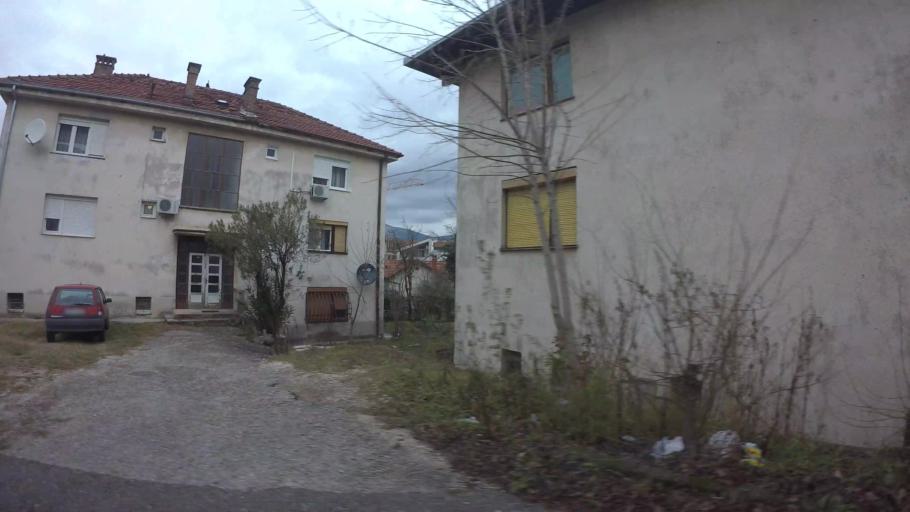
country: BA
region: Federation of Bosnia and Herzegovina
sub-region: Hercegovacko-Bosanski Kanton
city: Mostar
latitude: 43.3371
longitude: 17.7993
